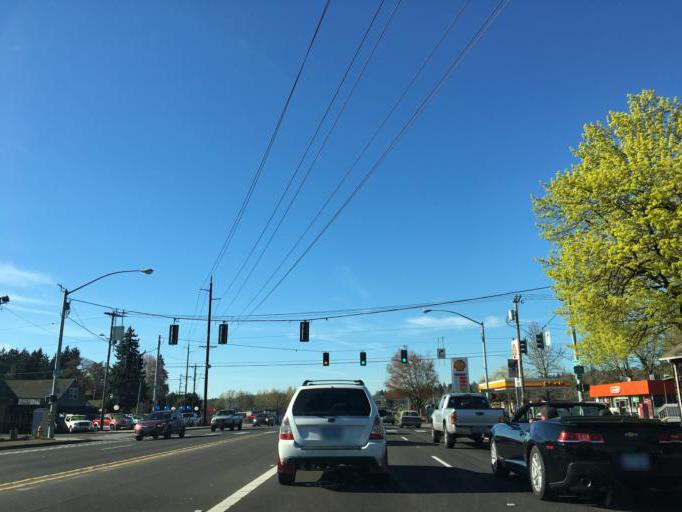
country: US
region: Oregon
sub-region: Clackamas County
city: Jennings Lodge
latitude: 45.3910
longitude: -122.6127
